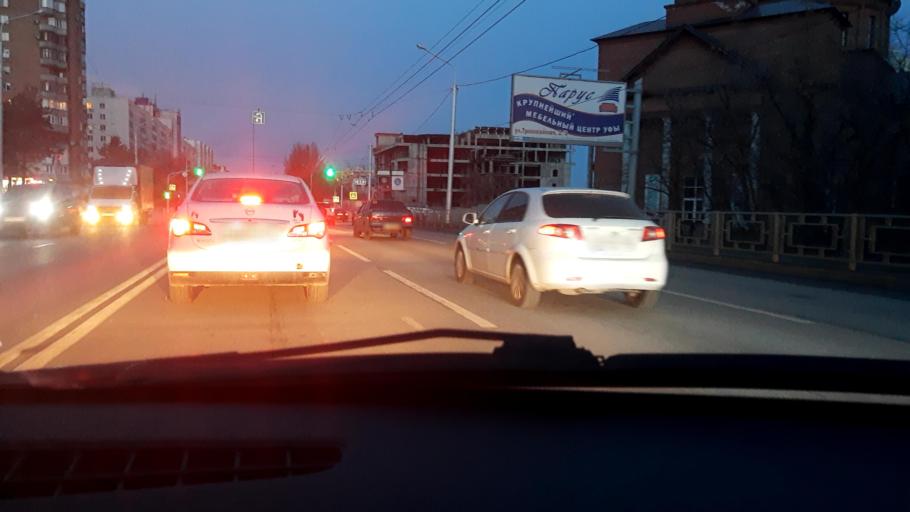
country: RU
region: Bashkortostan
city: Ufa
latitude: 54.7639
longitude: 56.0243
